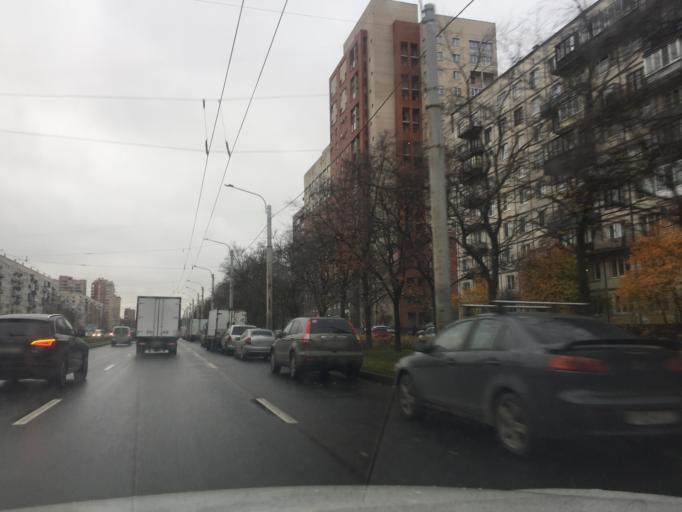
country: RU
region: St.-Petersburg
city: Grazhdanka
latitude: 60.0429
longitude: 30.4012
